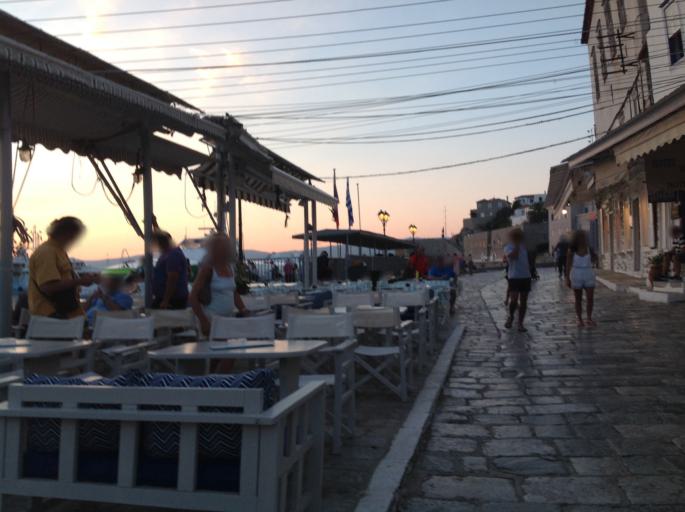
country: GR
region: Attica
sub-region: Nomos Piraios
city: Ydra
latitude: 37.3504
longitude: 23.4669
